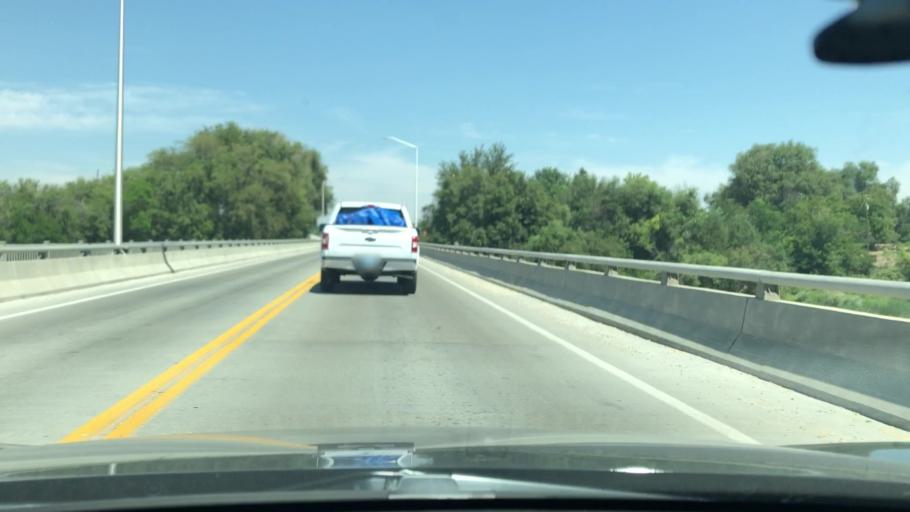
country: US
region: Idaho
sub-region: Owyhee County
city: Homedale
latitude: 43.6192
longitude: -116.9234
